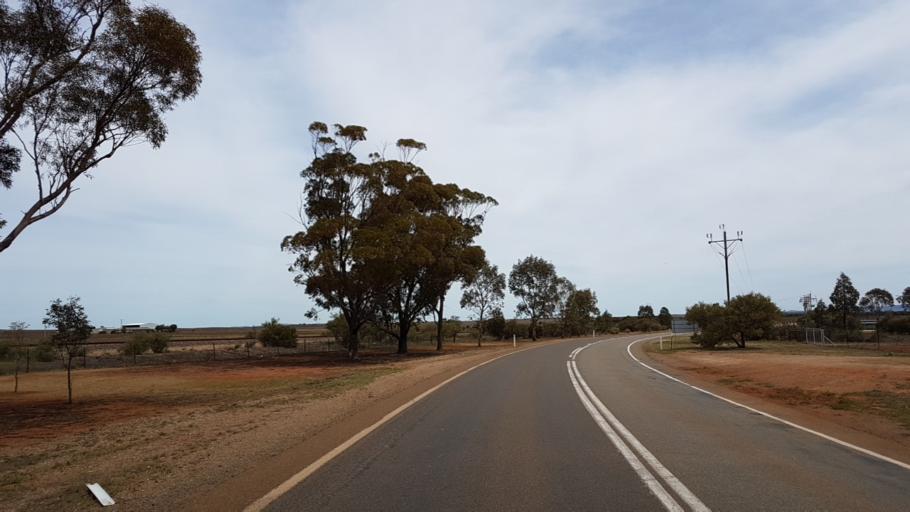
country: AU
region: South Australia
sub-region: Peterborough
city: Peterborough
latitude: -32.9787
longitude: 138.8190
